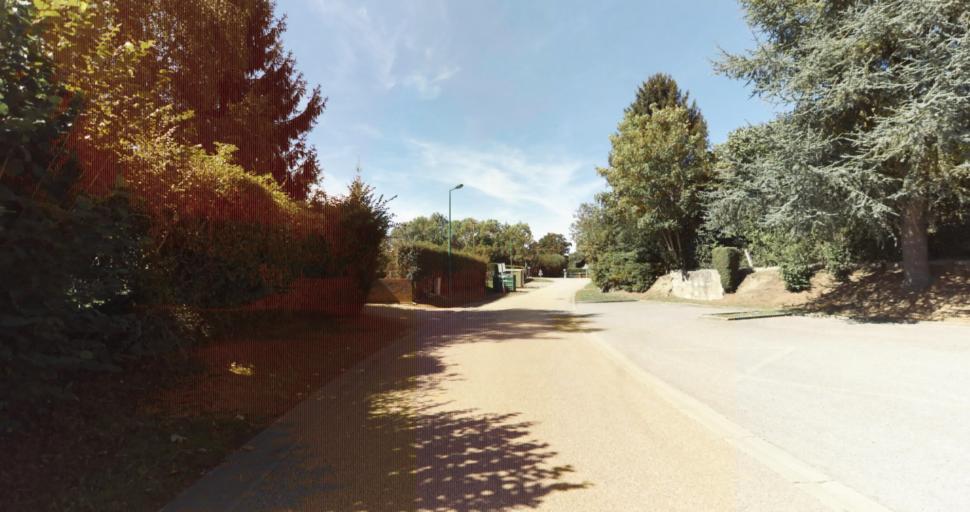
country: FR
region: Lower Normandy
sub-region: Departement de l'Orne
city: Gace
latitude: 48.7683
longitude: 0.2624
